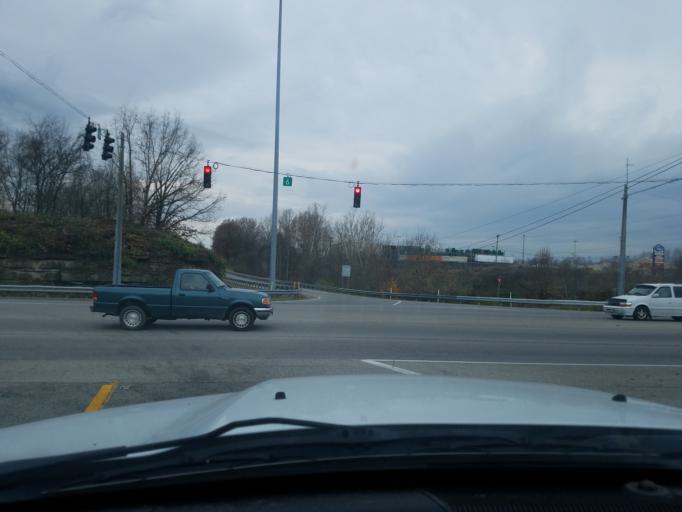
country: US
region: Kentucky
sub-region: Rowan County
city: Morehead
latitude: 38.1931
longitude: -83.4791
